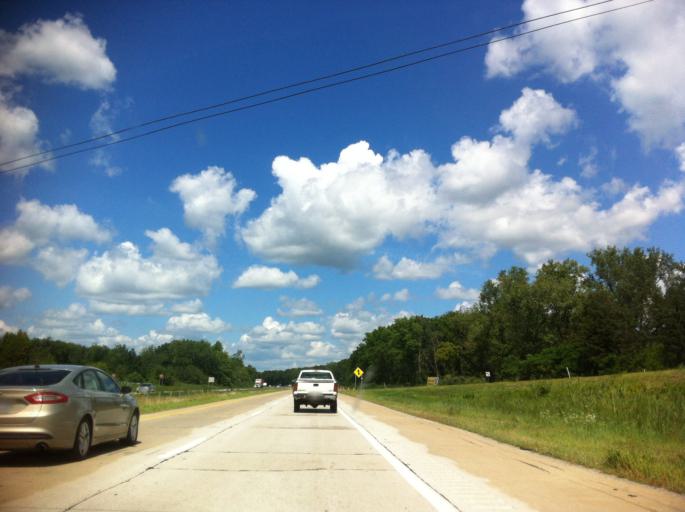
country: US
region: Michigan
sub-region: Monroe County
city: Petersburg
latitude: 41.8420
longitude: -83.6699
